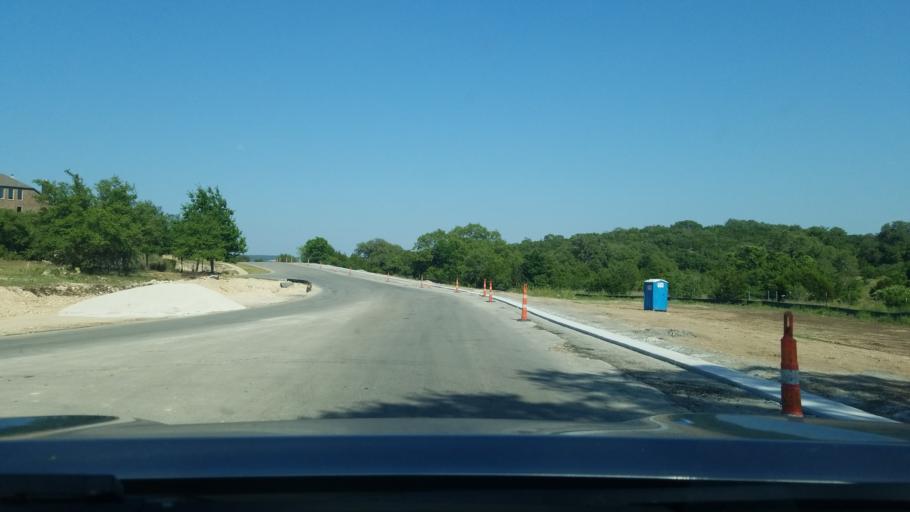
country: US
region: Texas
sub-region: Comal County
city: Bulverde
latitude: 29.7693
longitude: -98.4252
